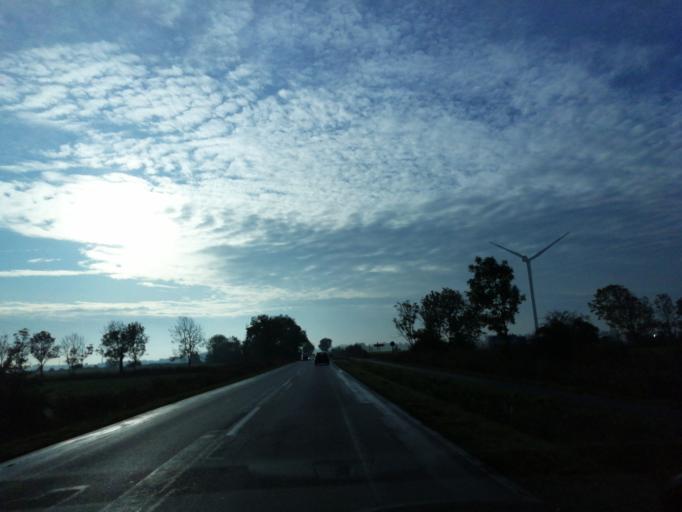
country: DE
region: Lower Saxony
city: Fedderwarden
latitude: 53.6120
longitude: 8.0412
